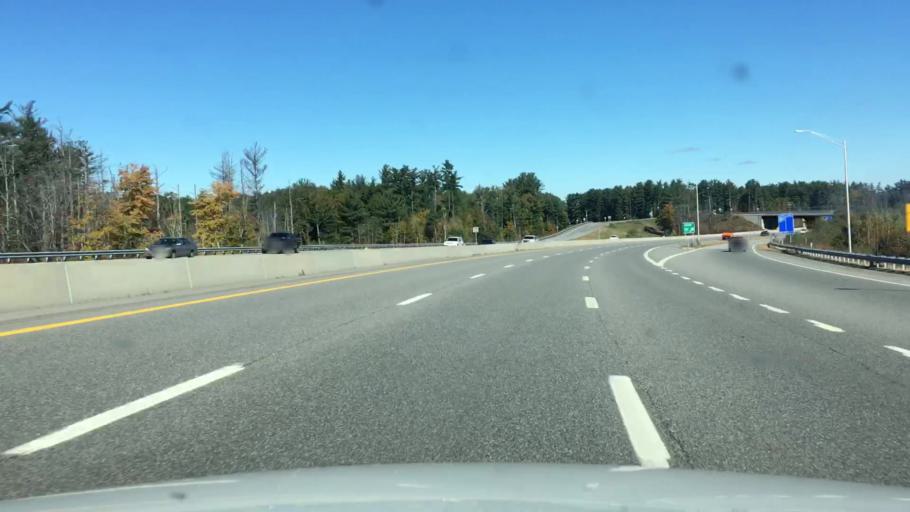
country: US
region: New Hampshire
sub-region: Strafford County
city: Rochester
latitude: 43.3146
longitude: -70.9963
